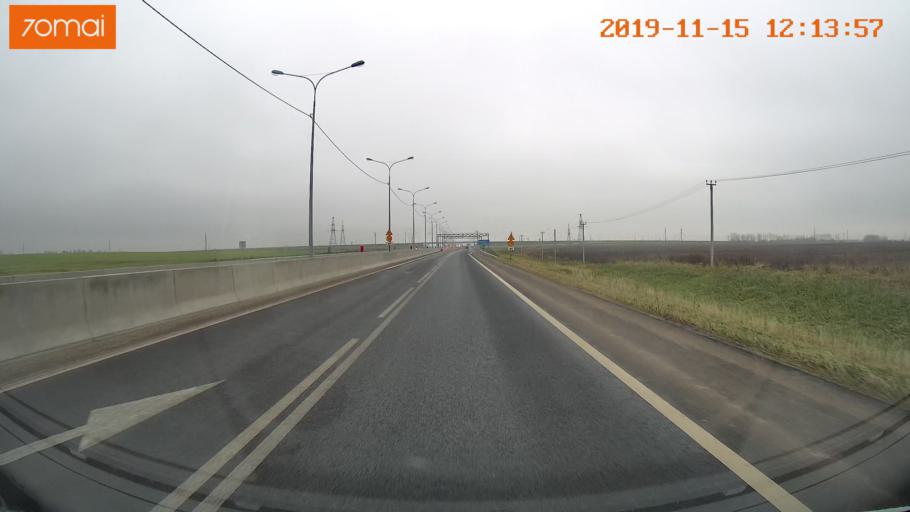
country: RU
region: Vologda
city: Vologda
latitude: 59.1617
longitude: 39.7996
